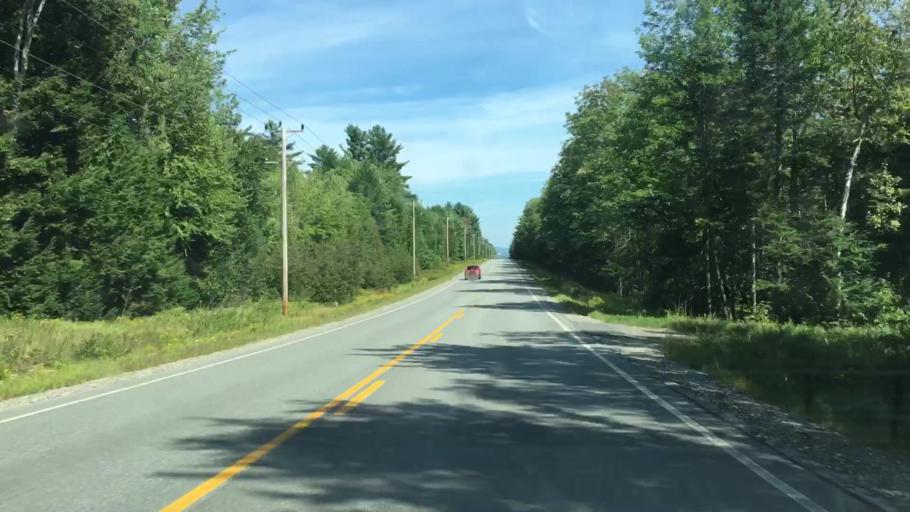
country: US
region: Maine
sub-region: Penobscot County
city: Howland
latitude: 45.2313
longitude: -68.7662
